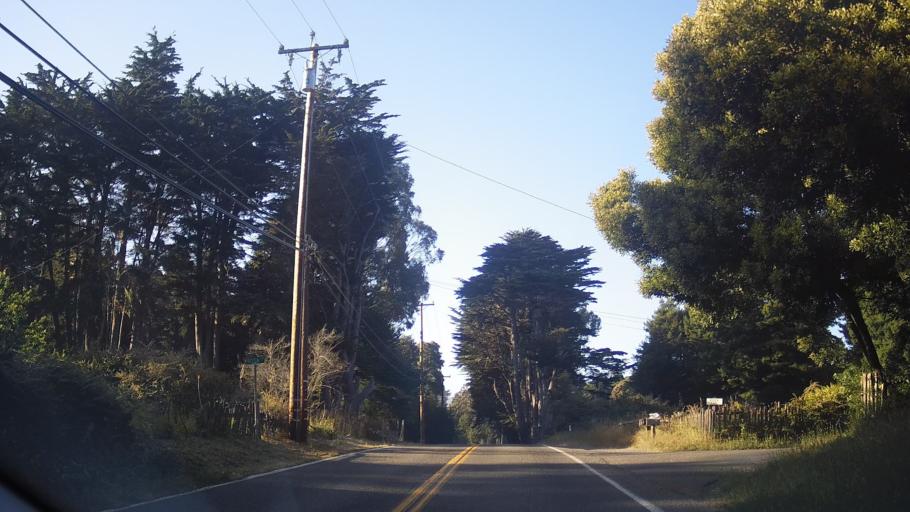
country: US
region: California
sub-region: Mendocino County
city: Fort Bragg
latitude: 39.5191
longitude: -123.7621
